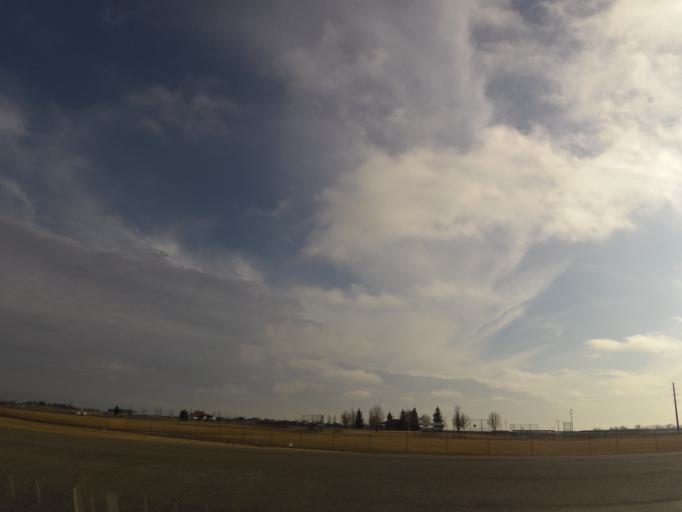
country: US
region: North Dakota
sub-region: Grand Forks County
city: Grand Forks
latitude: 47.8750
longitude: -97.0643
